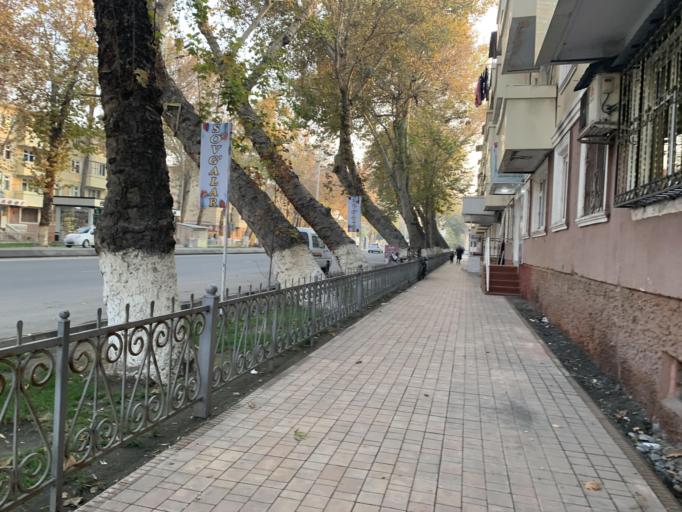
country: UZ
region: Fergana
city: Qo`qon
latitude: 40.5296
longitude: 70.9388
